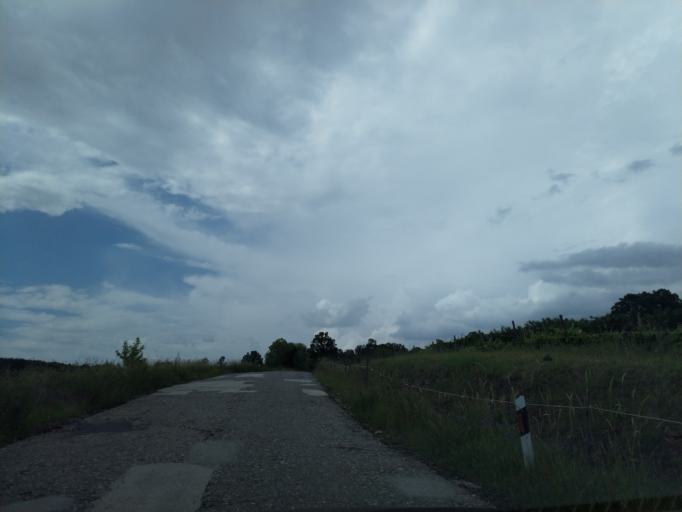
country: RS
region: Central Serbia
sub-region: Zajecarski Okrug
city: Boljevac
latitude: 43.8832
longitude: 21.9713
